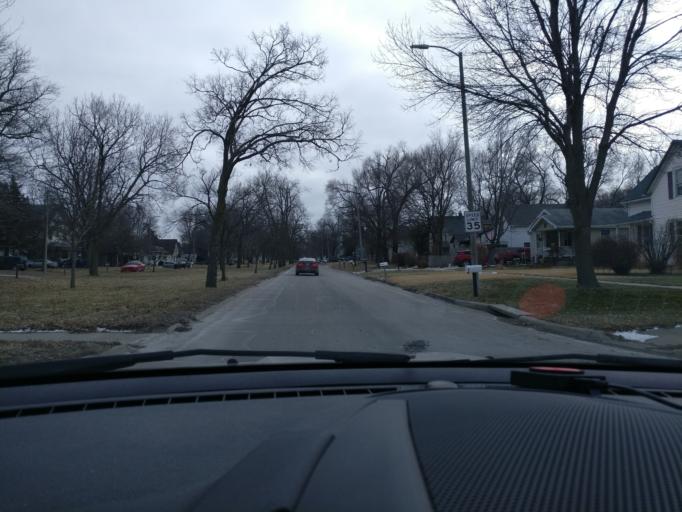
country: US
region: Nebraska
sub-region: Lancaster County
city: Lincoln
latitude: 40.8560
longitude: -96.6401
